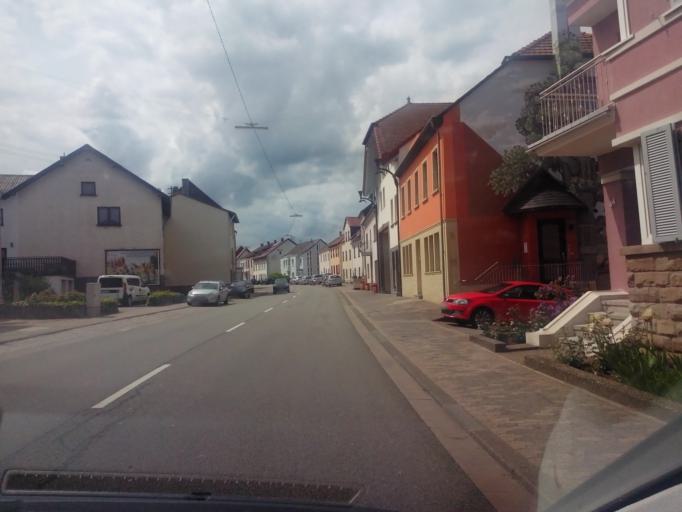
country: DE
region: Saarland
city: Eppelborn
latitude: 49.4054
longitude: 6.9620
